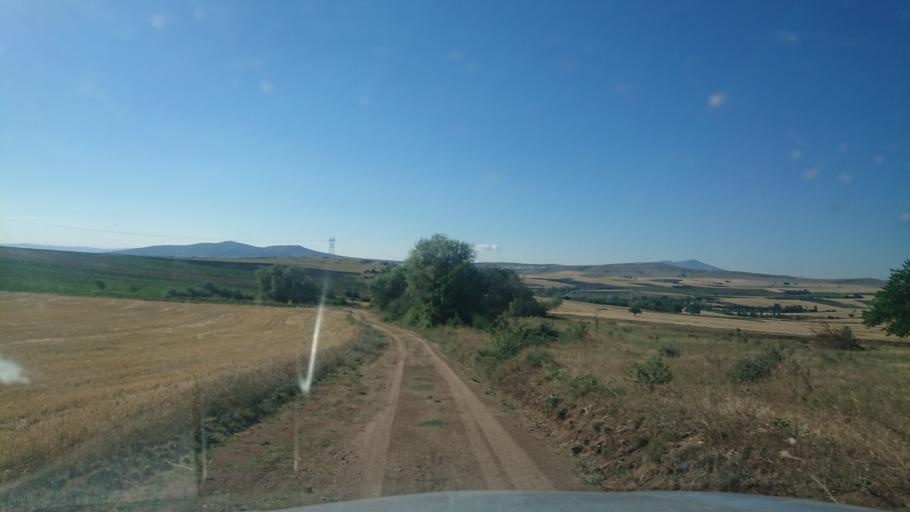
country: TR
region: Aksaray
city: Agacoren
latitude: 38.8338
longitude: 33.9396
